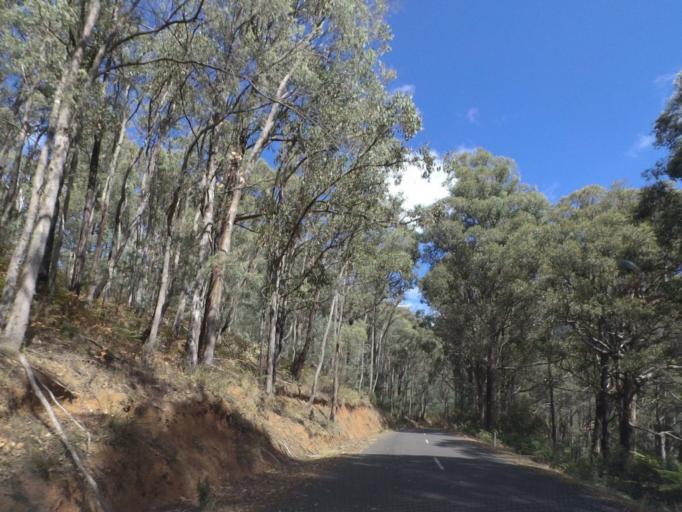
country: AU
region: Victoria
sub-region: Murrindindi
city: Alexandra
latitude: -37.3276
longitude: 145.9421
